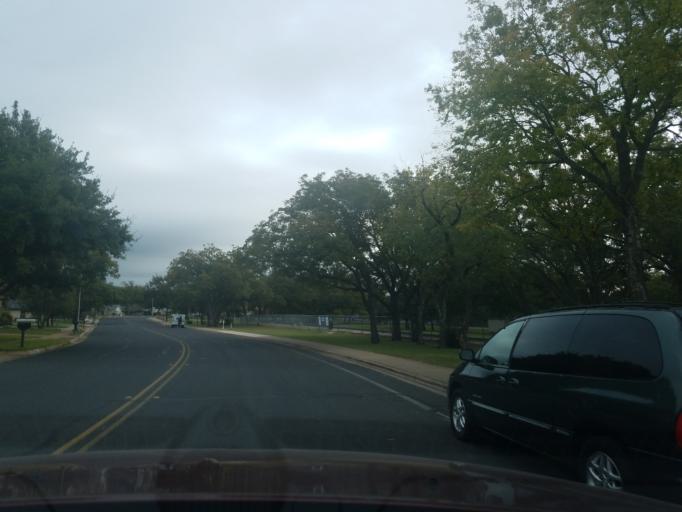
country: US
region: Texas
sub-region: Williamson County
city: Anderson Mill
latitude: 30.4577
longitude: -97.8059
